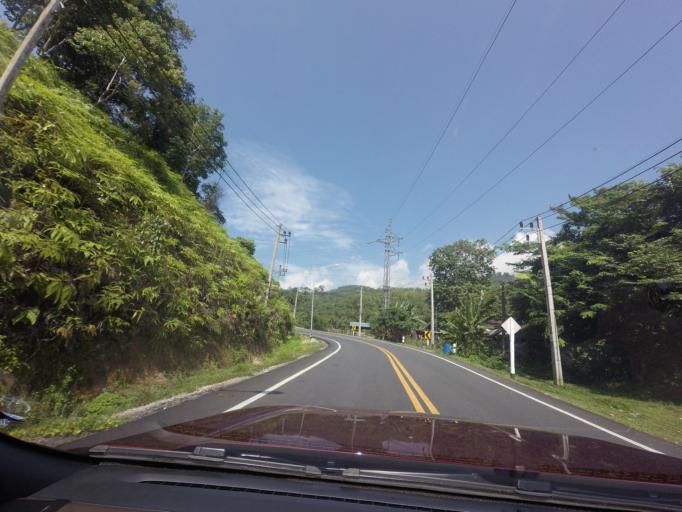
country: TH
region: Yala
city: Betong
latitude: 5.9072
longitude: 101.1490
